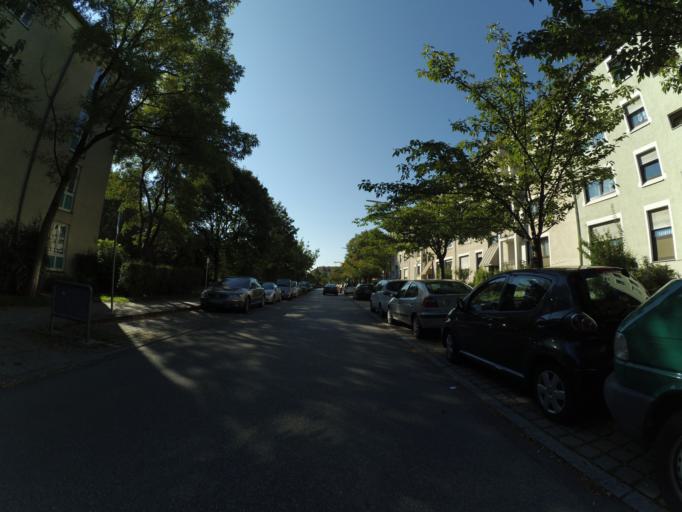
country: DE
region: Bavaria
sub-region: Upper Bavaria
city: Bogenhausen
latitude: 48.1840
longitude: 11.5831
